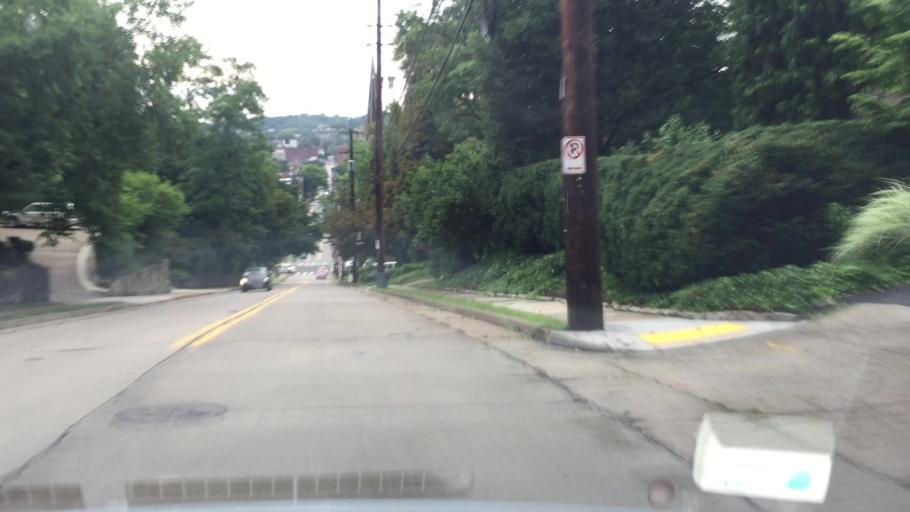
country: US
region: Pennsylvania
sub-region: Allegheny County
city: Bloomfield
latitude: 40.4480
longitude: -79.9285
